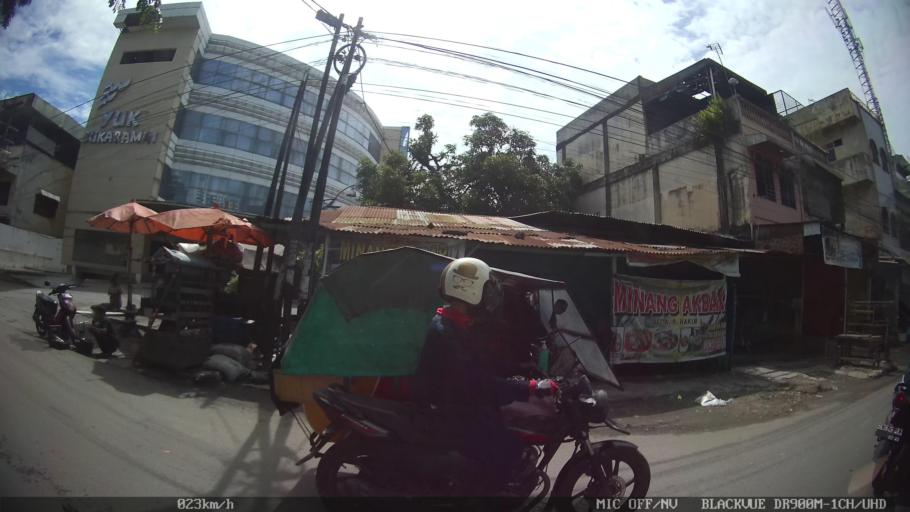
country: ID
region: North Sumatra
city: Medan
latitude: 3.5875
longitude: 98.7064
